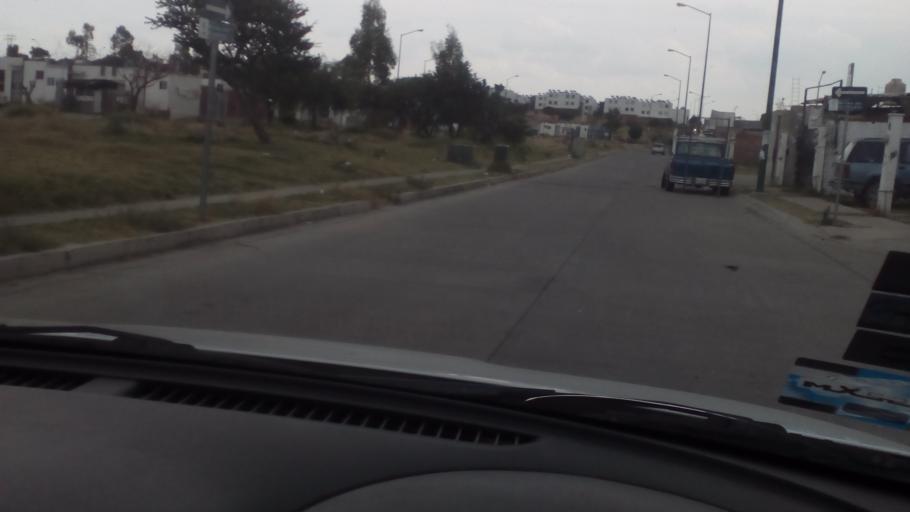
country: MX
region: Guanajuato
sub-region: Leon
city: Fraccionamiento Paseo de las Torres
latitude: 21.1908
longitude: -101.7659
